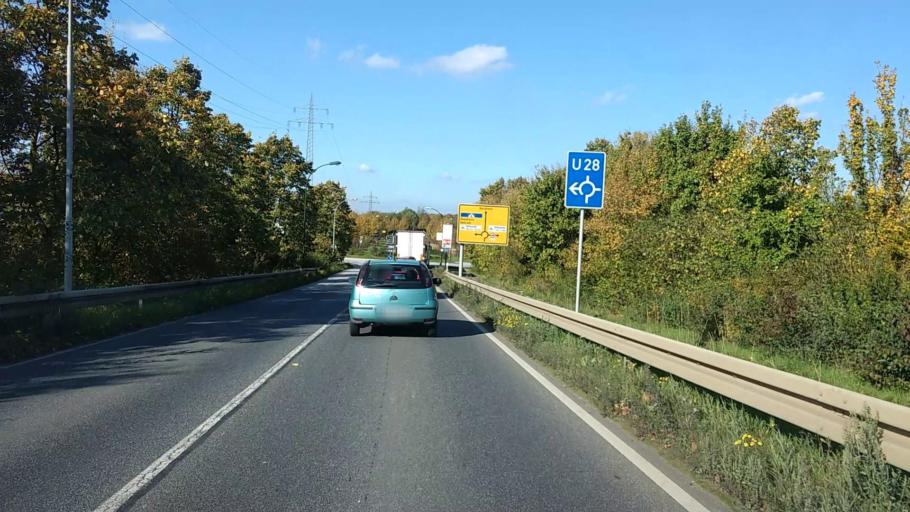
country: DE
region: North Rhine-Westphalia
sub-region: Regierungsbezirk Koln
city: Kerpen
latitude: 50.8967
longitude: 6.6604
